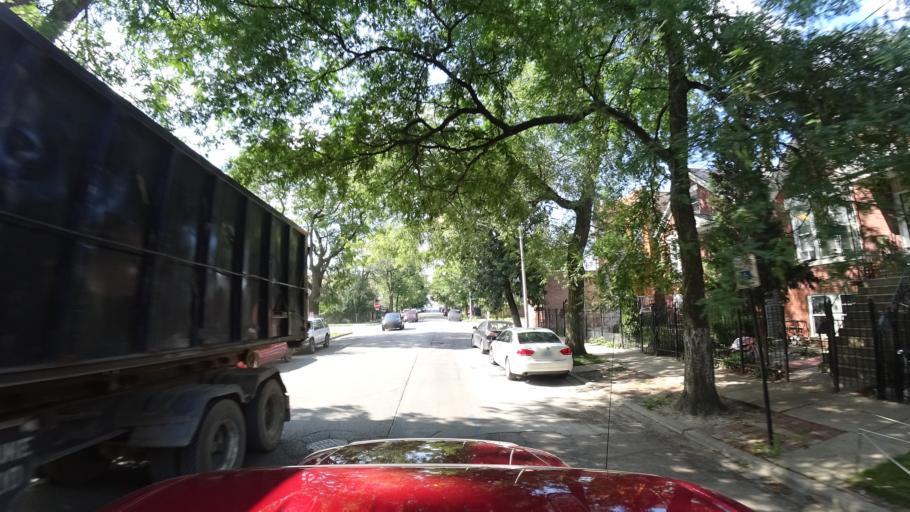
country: US
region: Illinois
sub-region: Cook County
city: Cicero
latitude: 41.8357
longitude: -87.7170
